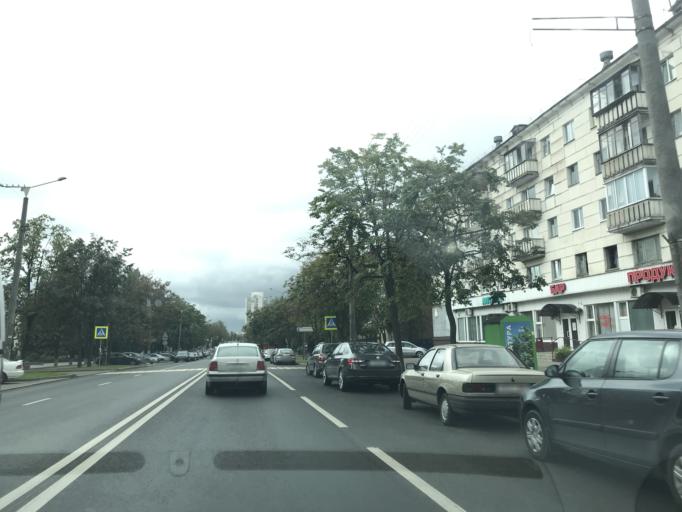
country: BY
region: Minsk
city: Minsk
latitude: 53.9307
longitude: 27.6239
